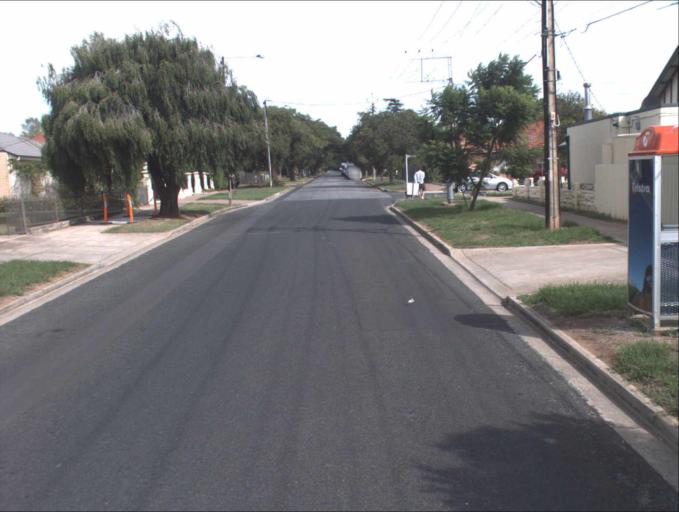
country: AU
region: South Australia
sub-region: Port Adelaide Enfield
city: Blair Athol
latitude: -34.8697
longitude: 138.5978
